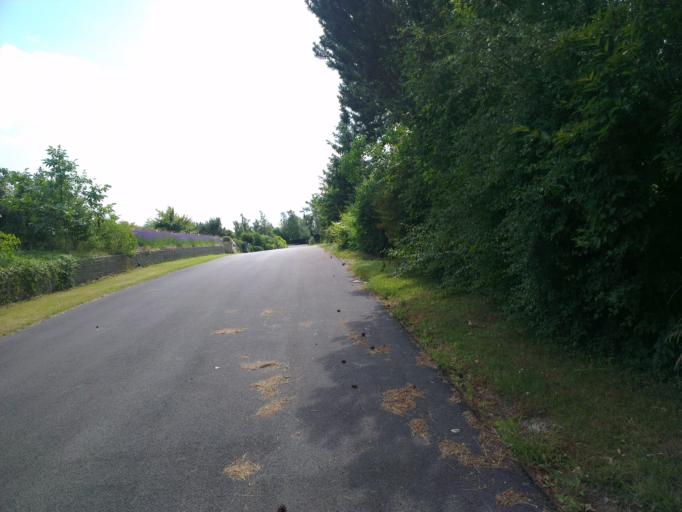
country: DK
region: Zealand
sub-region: Lejre Kommune
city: Ejby
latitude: 55.7503
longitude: 11.8642
